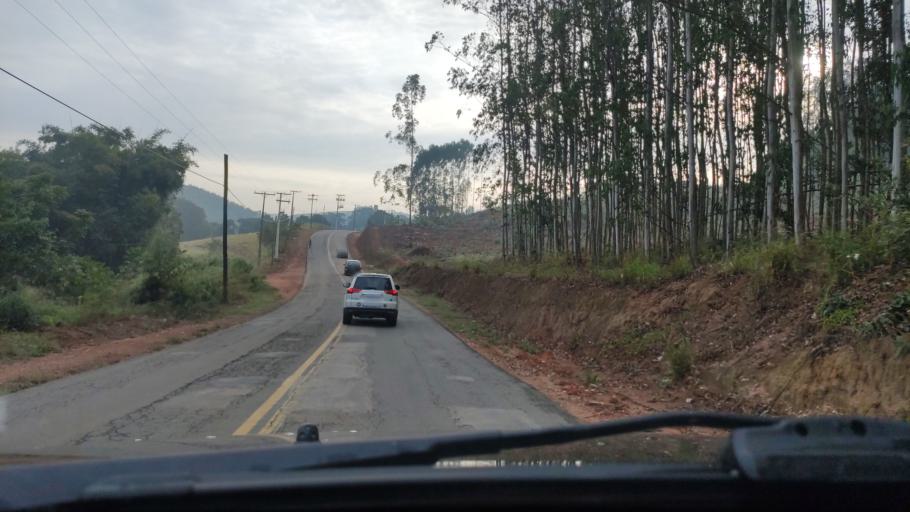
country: BR
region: Sao Paulo
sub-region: Jarinu
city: Jarinu
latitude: -23.1284
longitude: -46.7746
